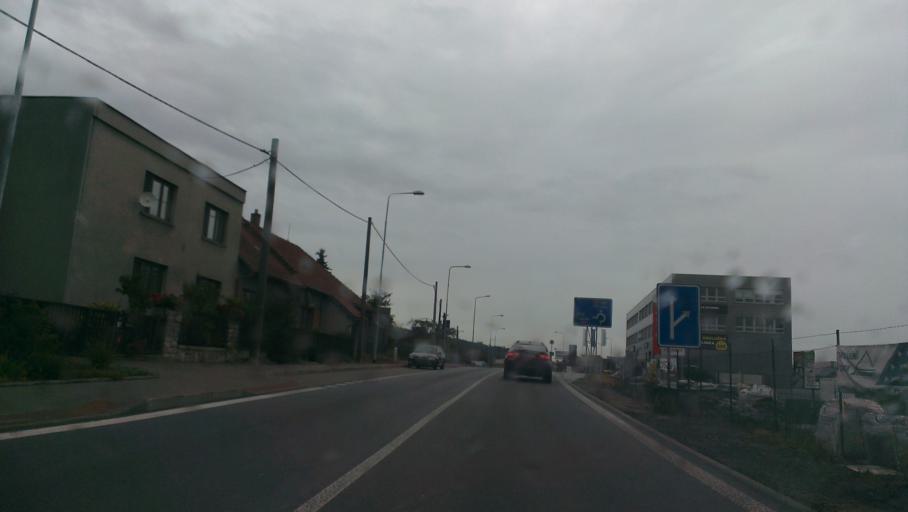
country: CZ
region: Vysocina
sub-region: Okres Zd'ar nad Sazavou
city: Velke Mezirici
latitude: 49.3478
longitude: 16.0359
